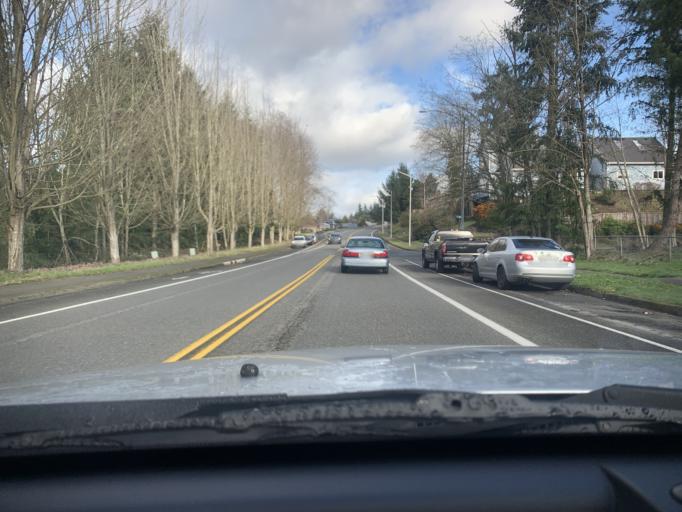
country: US
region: Washington
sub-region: Pierce County
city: Fircrest
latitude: 47.2734
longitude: -122.5238
